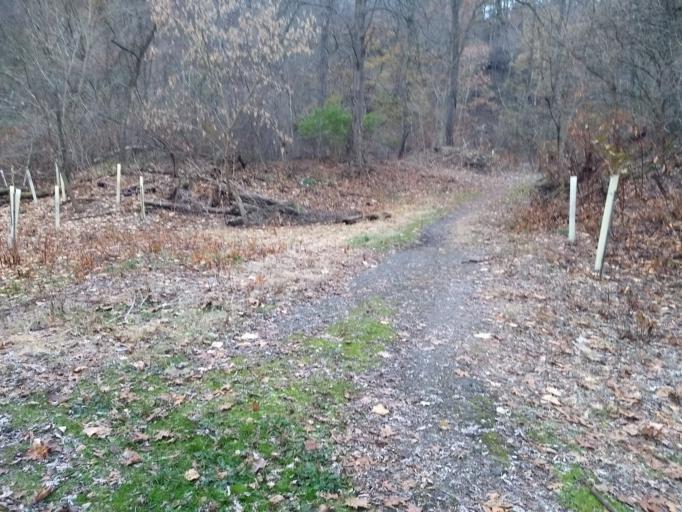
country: US
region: Pennsylvania
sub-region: Allegheny County
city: Green Tree
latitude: 40.4237
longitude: -80.0206
